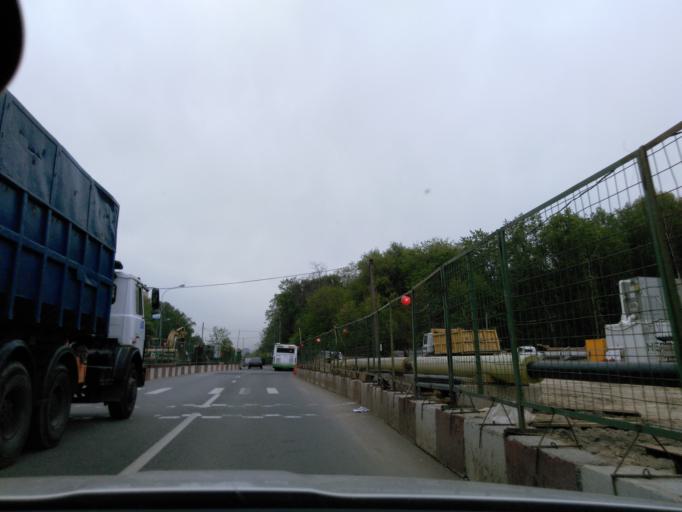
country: RU
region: Moskovskaya
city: Levoberezhnaya
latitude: 55.8773
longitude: 37.4819
